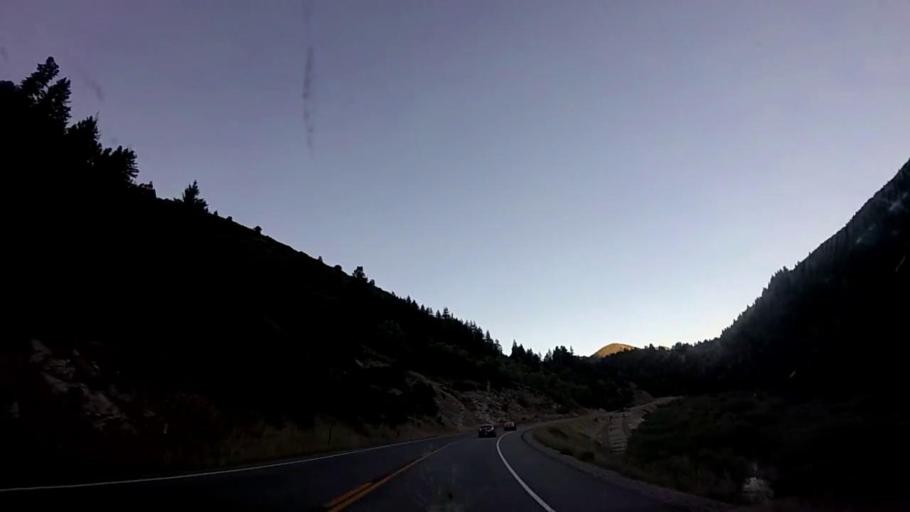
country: US
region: Utah
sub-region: Summit County
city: Summit Park
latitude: 40.6453
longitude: -111.6726
